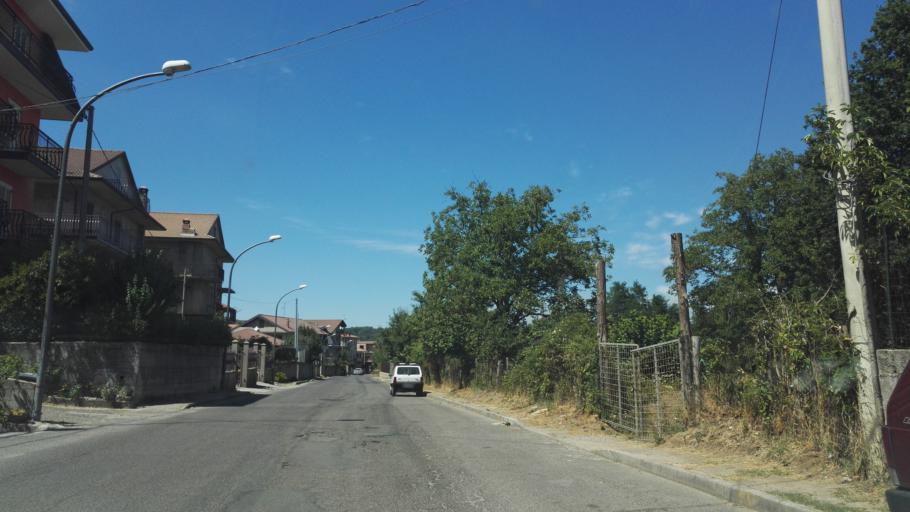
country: IT
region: Calabria
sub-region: Provincia di Vibo-Valentia
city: Serra San Bruno
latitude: 38.5666
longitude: 16.3283
